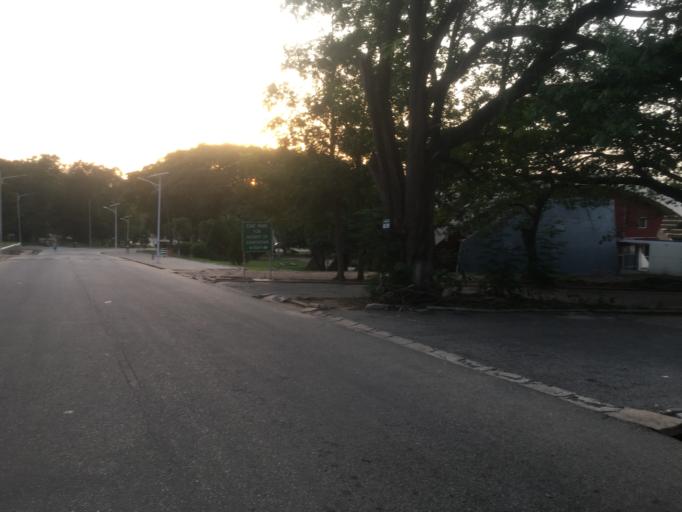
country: GH
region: Ashanti
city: Kumasi
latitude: 6.6749
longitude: -1.5663
